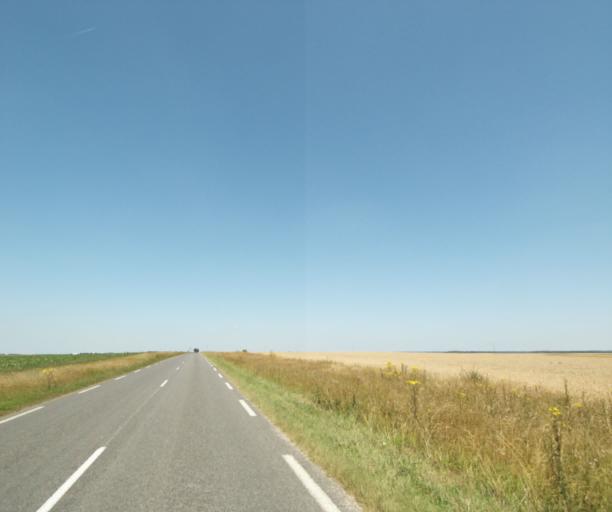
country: FR
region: Centre
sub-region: Departement du Loiret
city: Malesherbes
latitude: 48.3266
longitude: 2.4475
